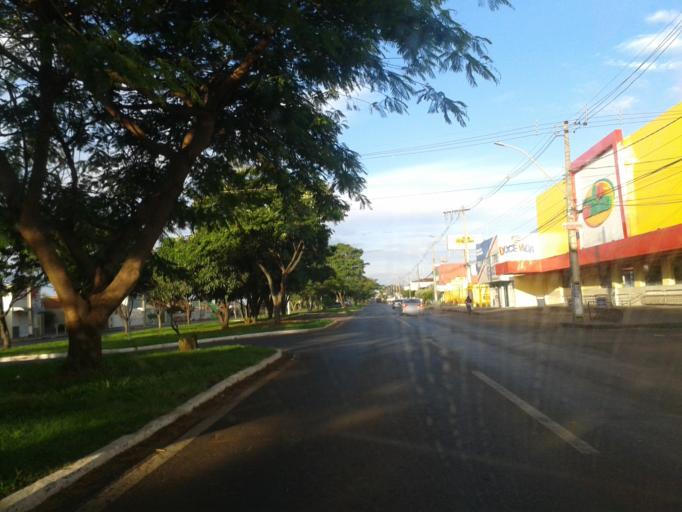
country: BR
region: Minas Gerais
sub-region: Araguari
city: Araguari
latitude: -18.6406
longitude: -48.1845
